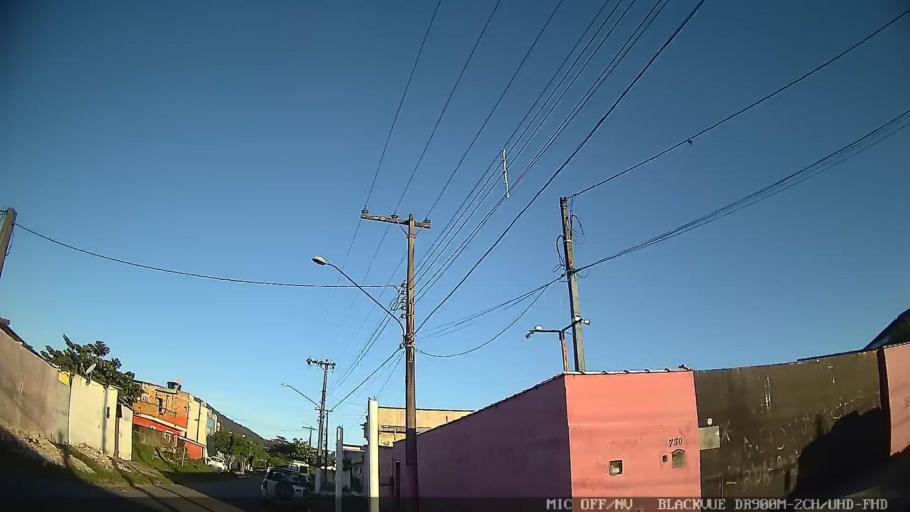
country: BR
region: Sao Paulo
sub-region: Guaruja
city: Guaruja
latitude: -23.9657
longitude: -46.2732
